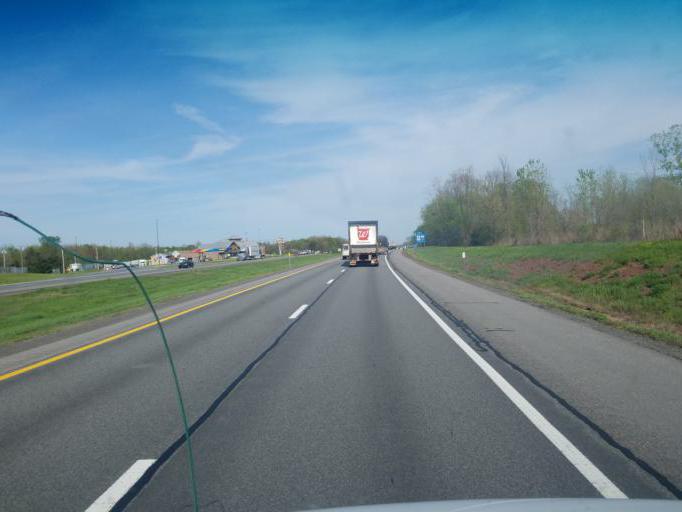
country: US
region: New York
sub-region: Madison County
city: Bolivar
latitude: 43.0956
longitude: -75.8454
